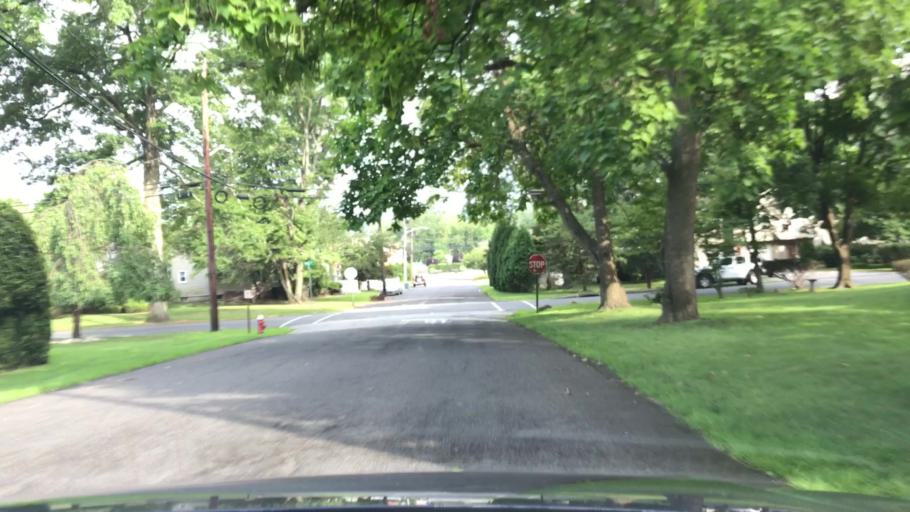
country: US
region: New Jersey
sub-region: Bergen County
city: Norwood
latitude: 40.9994
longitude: -73.9565
